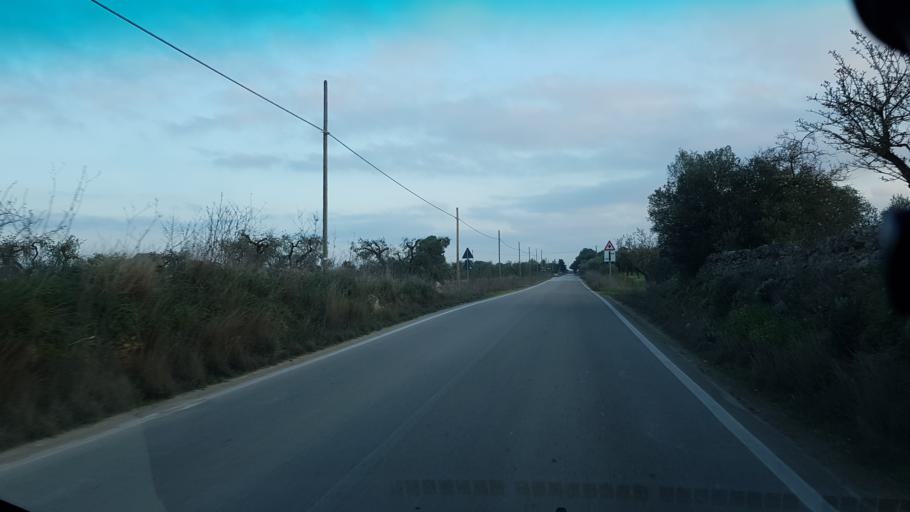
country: IT
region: Apulia
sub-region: Provincia di Brindisi
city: San Vito dei Normanni
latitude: 40.6474
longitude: 17.7759
